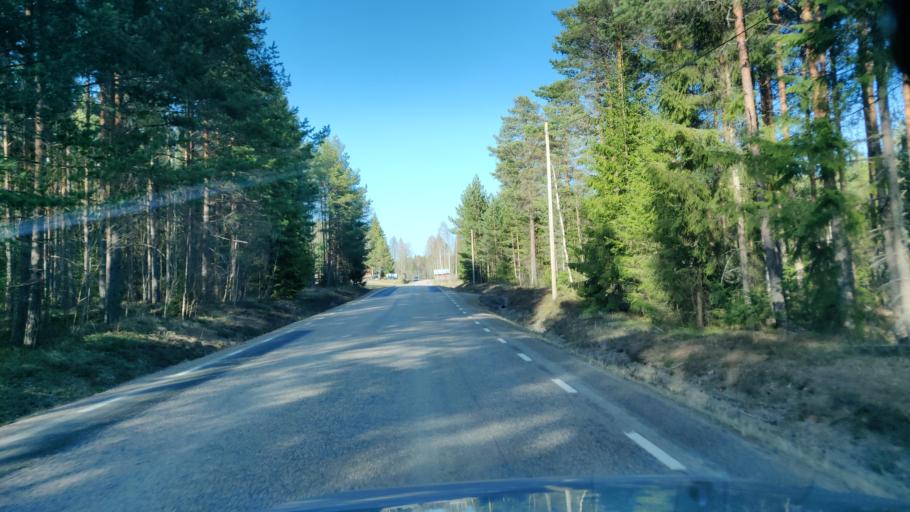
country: SE
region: Vaermland
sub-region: Sunne Kommun
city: Sunne
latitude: 59.9828
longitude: 13.2606
